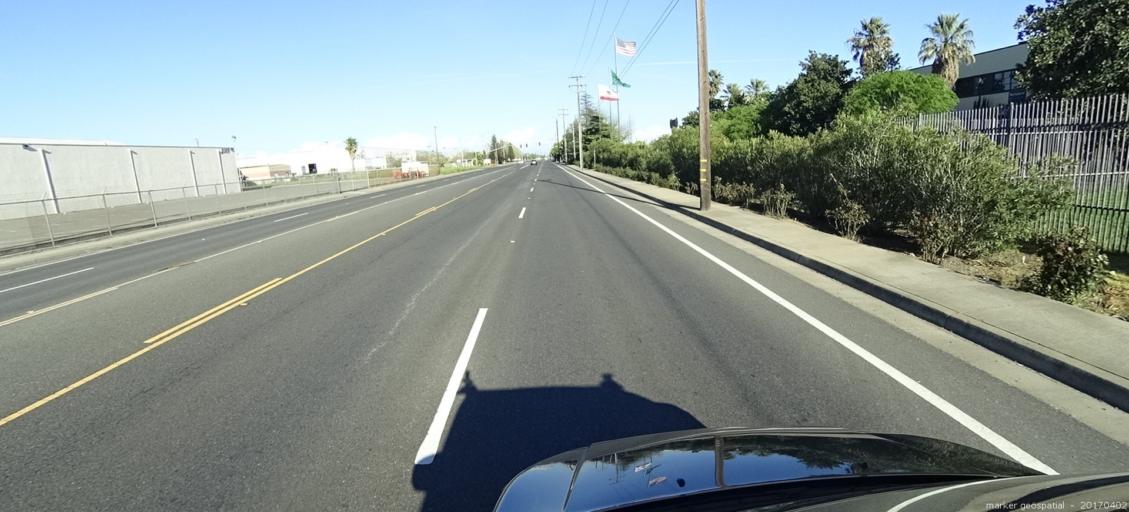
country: US
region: California
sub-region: Sacramento County
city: Florin
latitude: 38.5251
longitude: -121.3979
